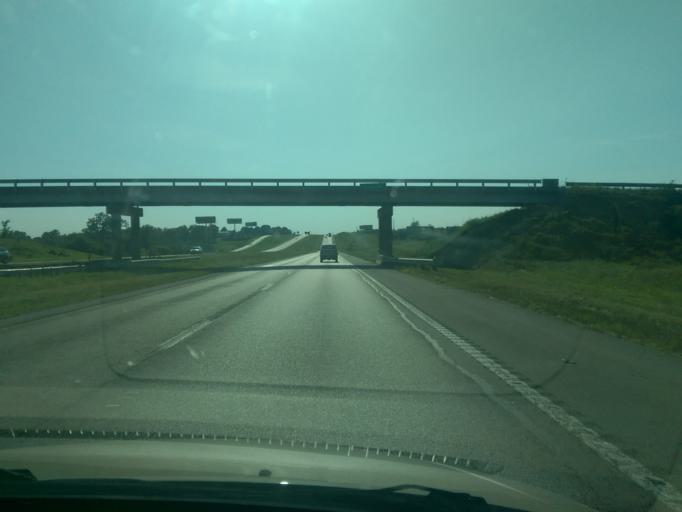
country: US
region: Missouri
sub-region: Lafayette County
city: Odessa
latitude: 39.0098
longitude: -94.0067
